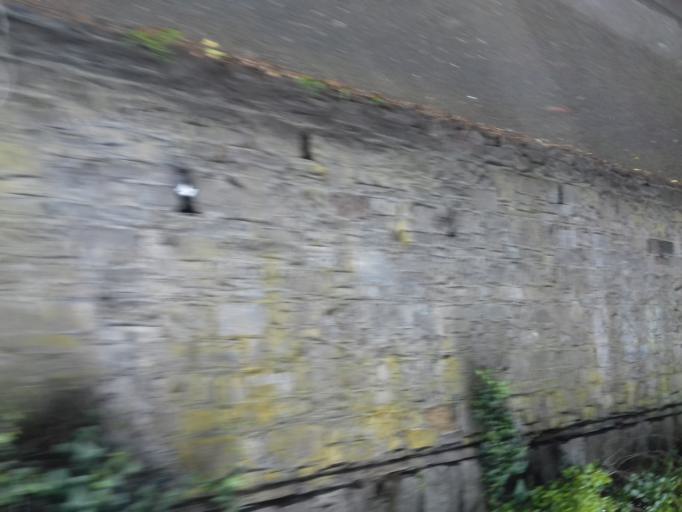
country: IE
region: Leinster
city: Crumlin
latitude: 53.3419
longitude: -6.3261
